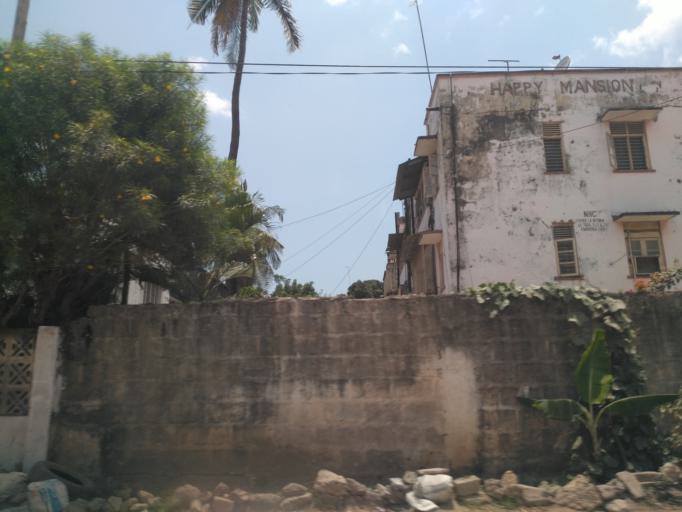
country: TZ
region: Dar es Salaam
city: Dar es Salaam
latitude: -6.8096
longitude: 39.2765
